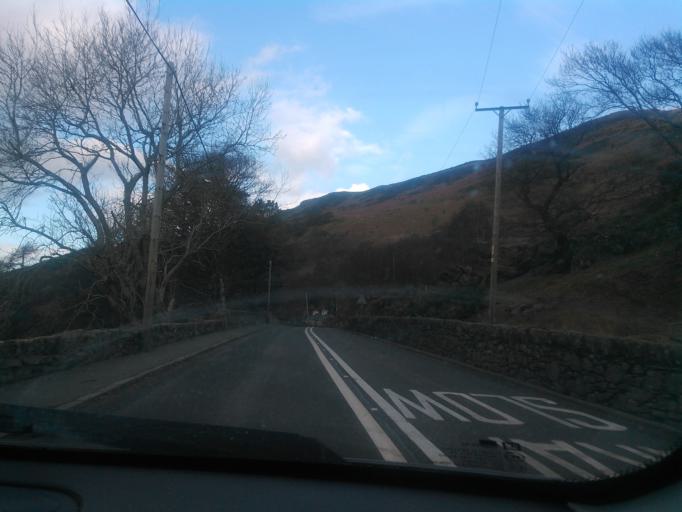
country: GB
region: Wales
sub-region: Gwynedd
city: Bethesda
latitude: 53.1592
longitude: -4.0444
